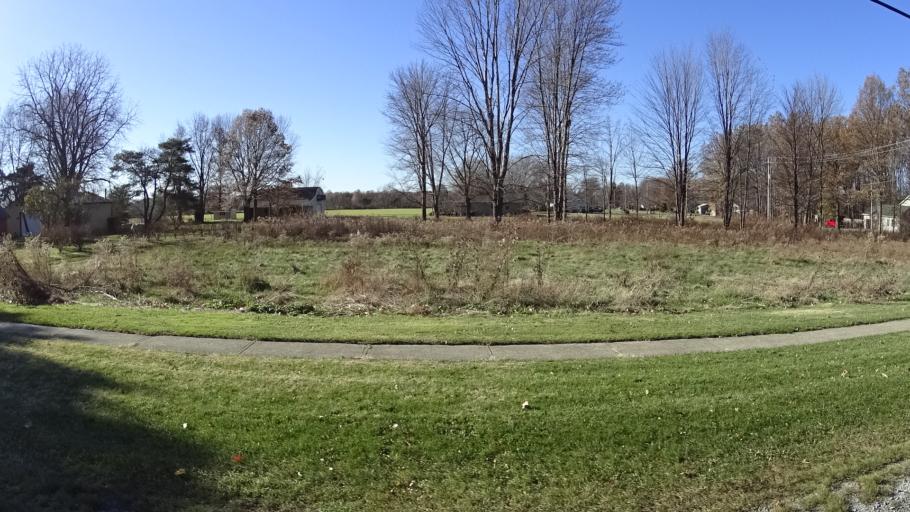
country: US
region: Ohio
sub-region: Lorain County
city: Avon Center
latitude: 41.4411
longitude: -82.0190
